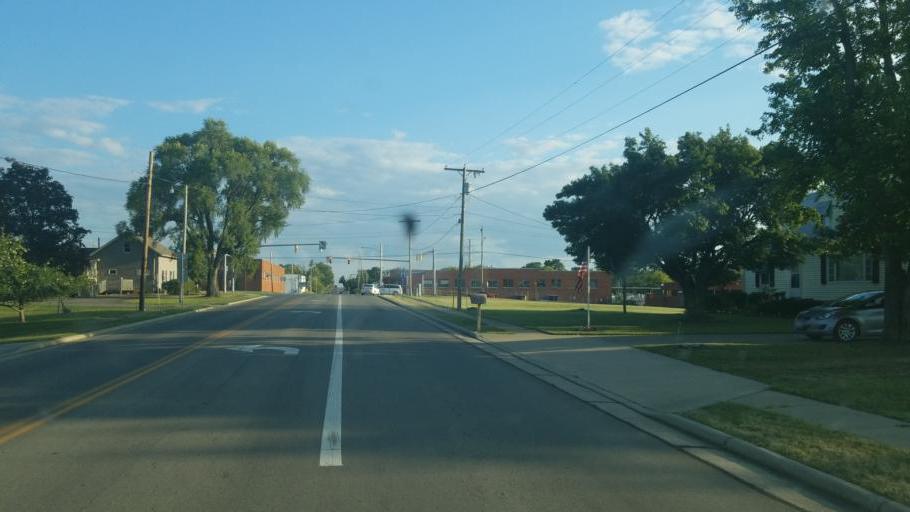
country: US
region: Ohio
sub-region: Huron County
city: Willard
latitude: 41.0539
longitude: -82.7162
